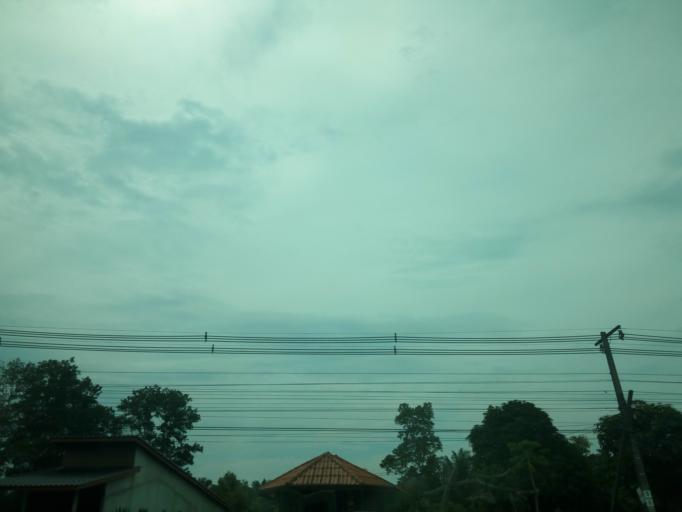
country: TH
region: Krabi
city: Khlong Thom
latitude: 7.9922
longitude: 99.1307
